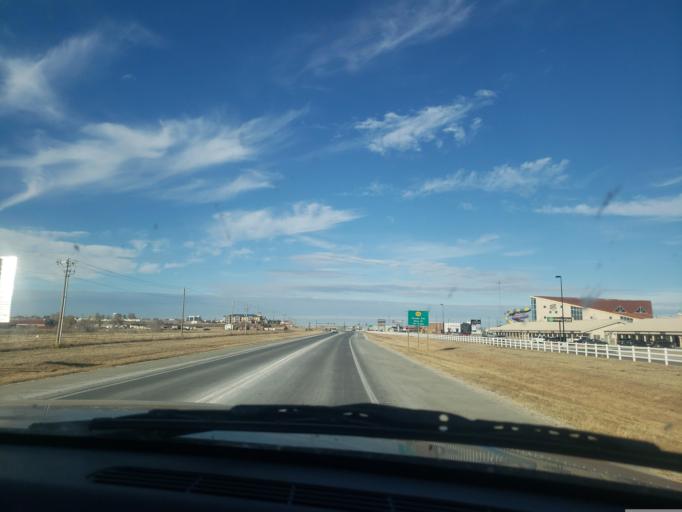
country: US
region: Kansas
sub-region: Finney County
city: Garden City
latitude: 37.9705
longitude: -100.8388
